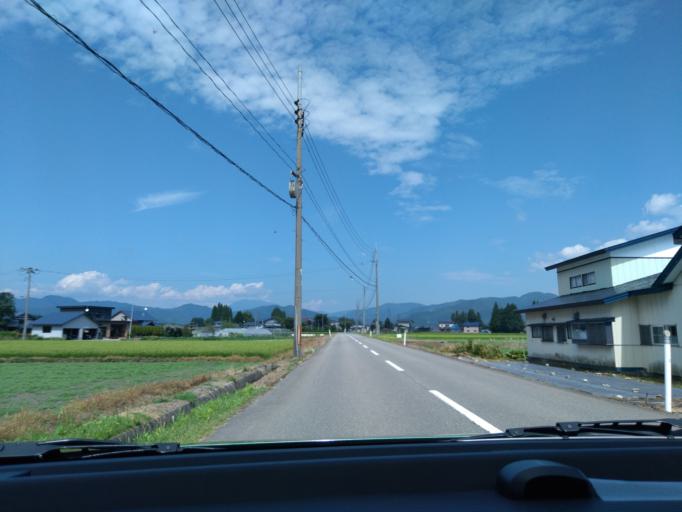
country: JP
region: Akita
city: Kakunodatemachi
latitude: 39.6034
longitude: 140.5877
